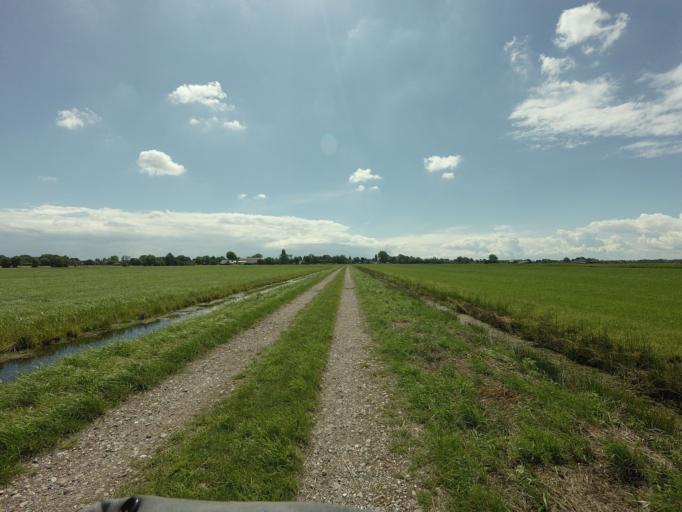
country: NL
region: South Holland
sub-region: Gemeente Schoonhoven
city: Schoonhoven
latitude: 51.9643
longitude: 4.8741
